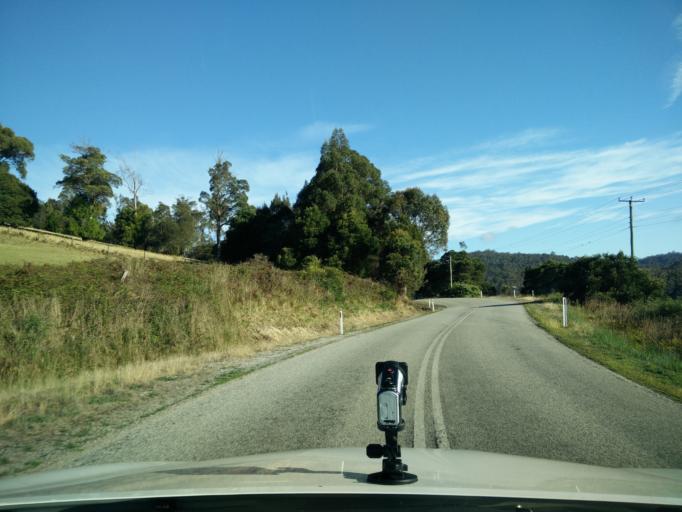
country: AU
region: Tasmania
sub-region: Break O'Day
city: St Helens
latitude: -41.2635
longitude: 148.0905
